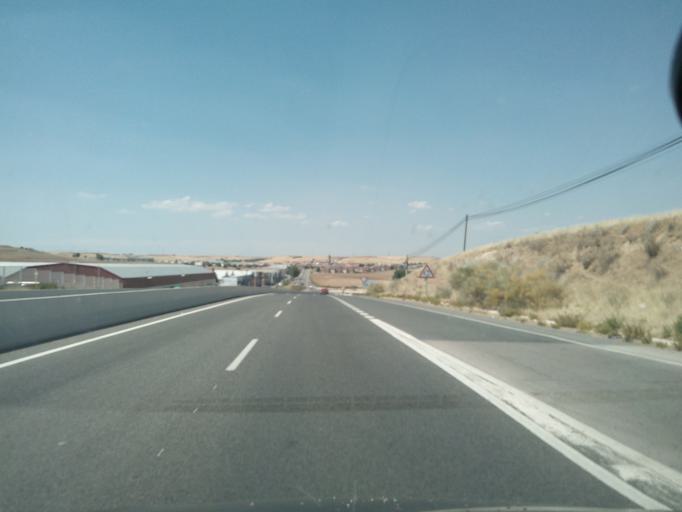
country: ES
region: Madrid
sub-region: Provincia de Madrid
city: Ajalvir
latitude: 40.5176
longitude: -3.4809
